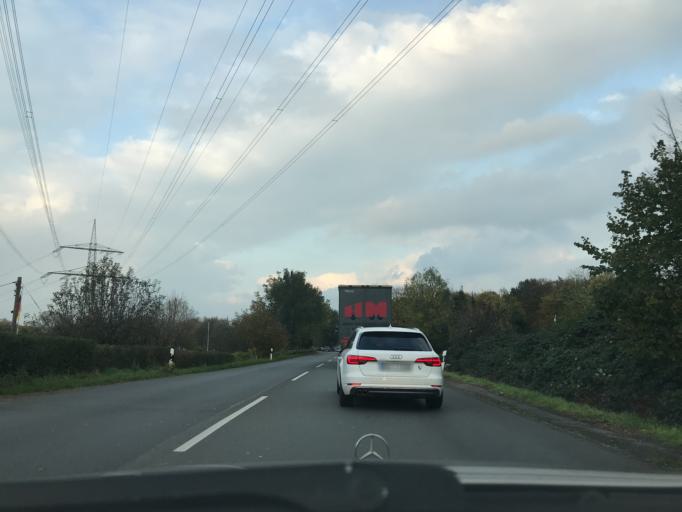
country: DE
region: North Rhine-Westphalia
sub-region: Regierungsbezirk Munster
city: Gelsenkirchen
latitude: 51.4948
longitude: 7.0981
